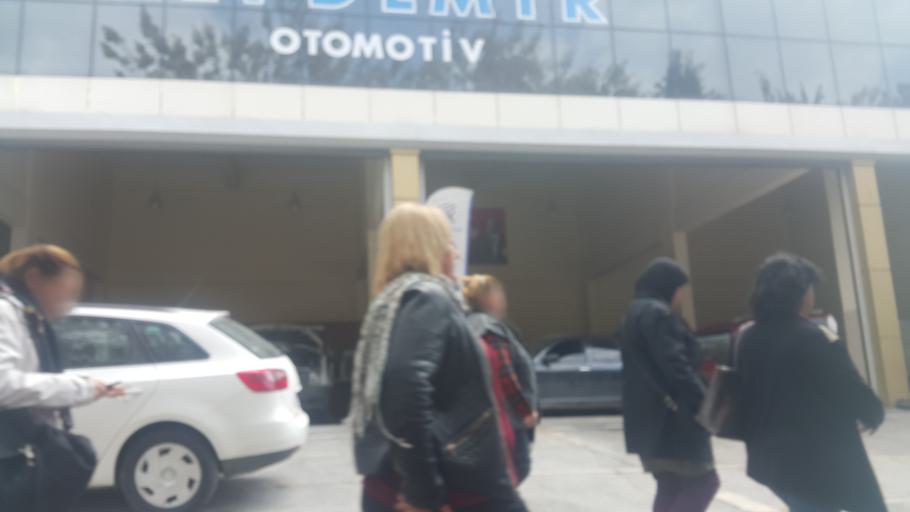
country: TR
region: Mersin
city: Mercin
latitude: 36.8163
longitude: 34.6051
